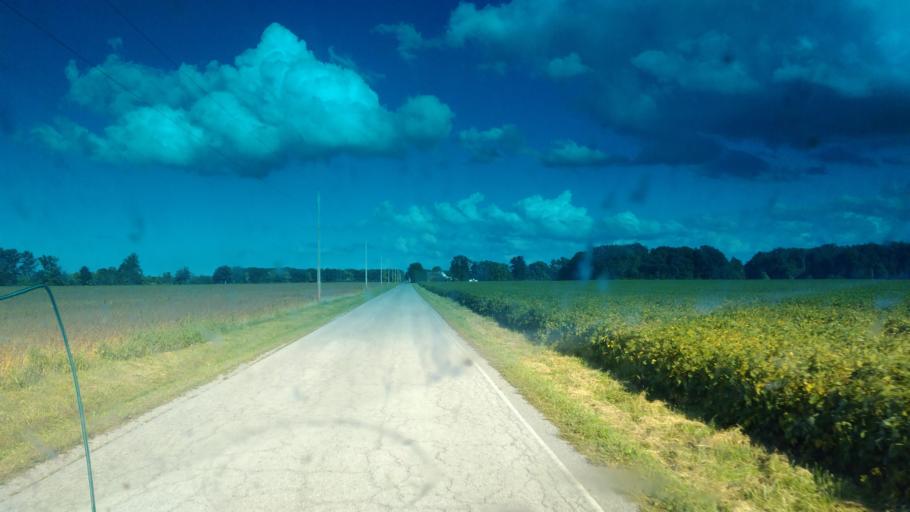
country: US
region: Ohio
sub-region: Hancock County
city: Arlington
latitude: 40.9361
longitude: -83.6975
